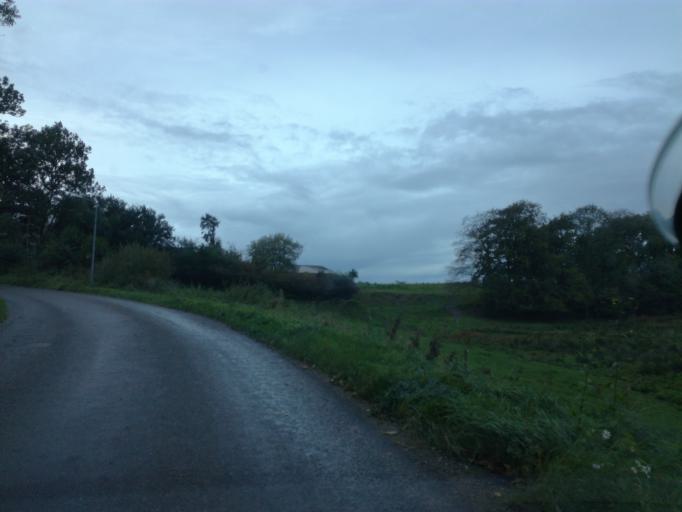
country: DK
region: South Denmark
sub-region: Fredericia Kommune
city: Fredericia
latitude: 55.6083
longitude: 9.7240
